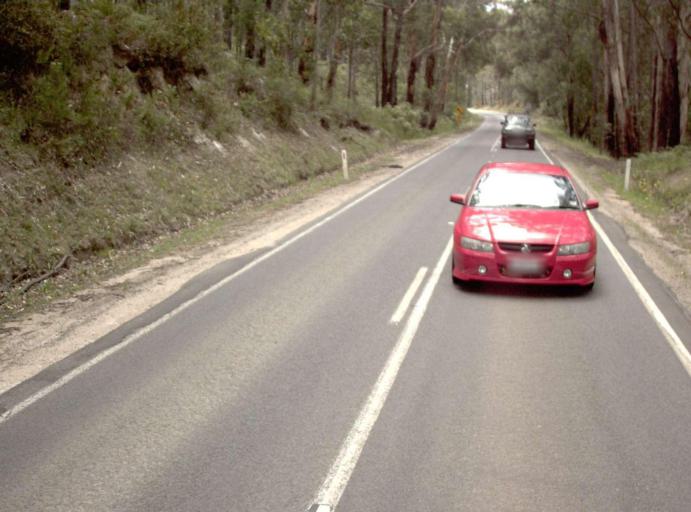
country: AU
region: Victoria
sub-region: Latrobe
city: Traralgon
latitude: -38.4231
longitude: 146.7455
